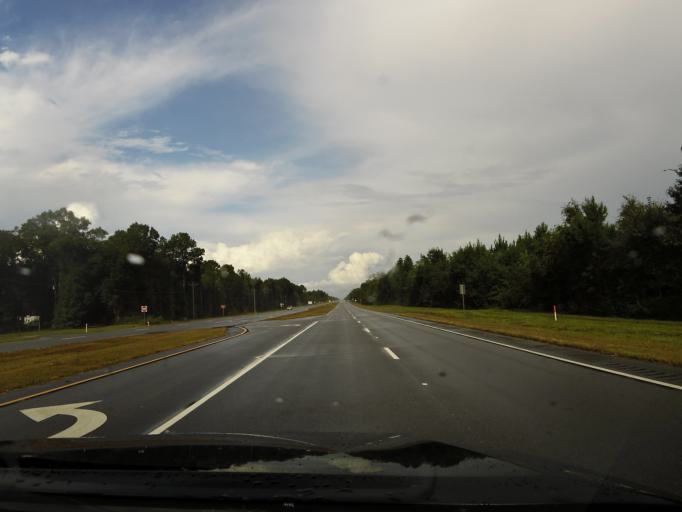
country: US
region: Georgia
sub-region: Long County
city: Ludowici
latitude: 31.7329
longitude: -81.7088
